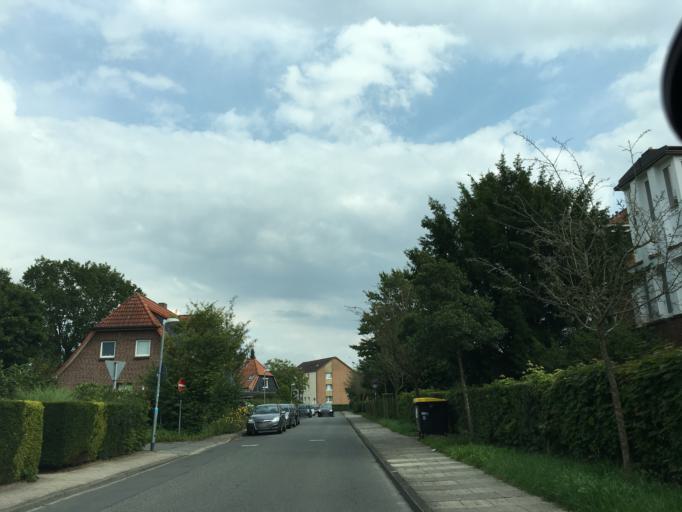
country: DE
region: Lower Saxony
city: Lueneburg
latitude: 53.2570
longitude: 10.3845
